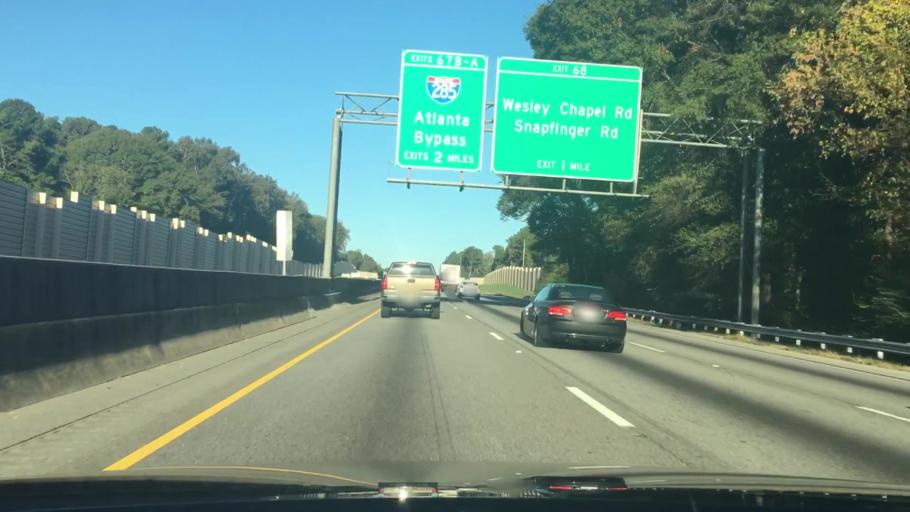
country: US
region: Georgia
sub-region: DeKalb County
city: Panthersville
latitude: 33.7059
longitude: -84.1998
